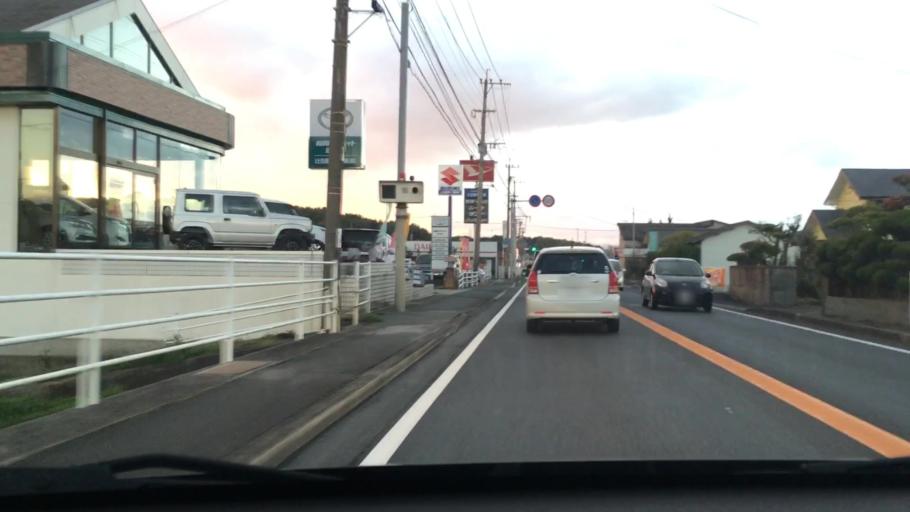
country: JP
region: Fukuoka
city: Shiida
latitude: 33.6322
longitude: 131.0808
